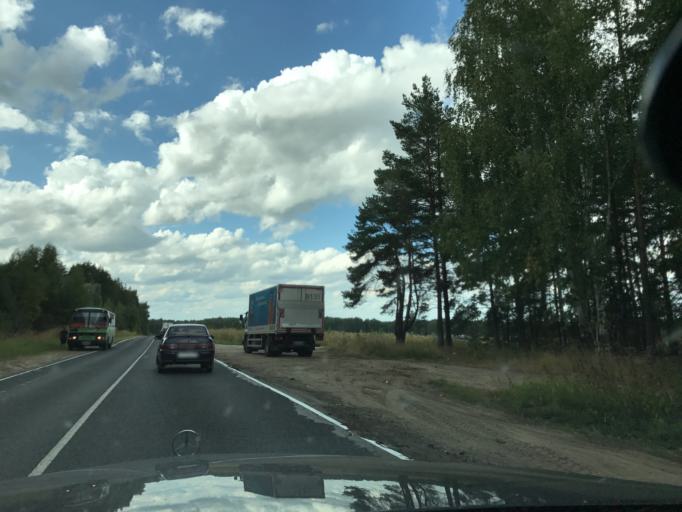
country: RU
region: Vladimir
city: Raduzhnyy
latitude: 55.9869
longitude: 40.2291
